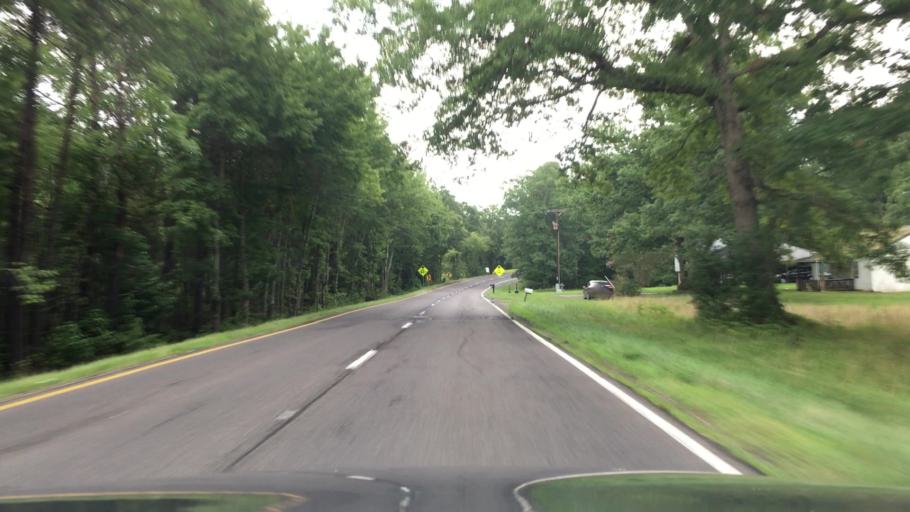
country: US
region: Virginia
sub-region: Spotsylvania County
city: Spotsylvania
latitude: 38.3192
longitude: -77.6931
